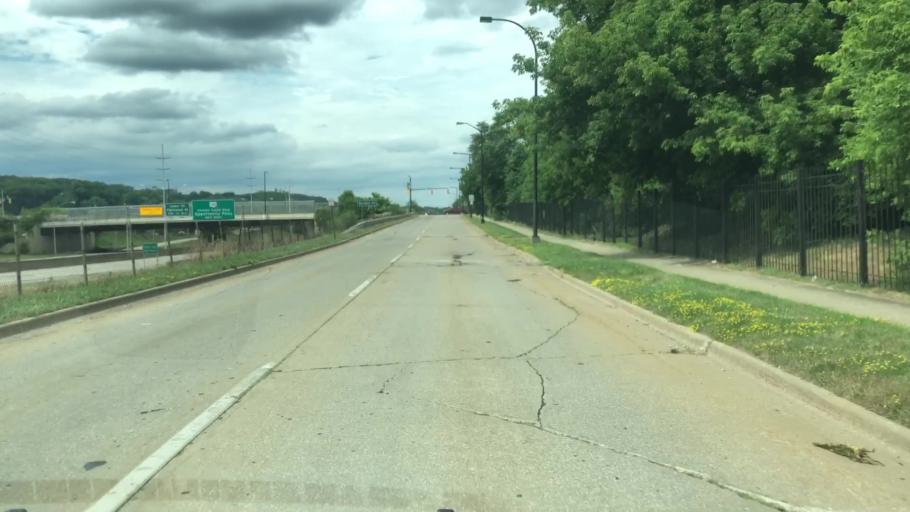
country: US
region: Ohio
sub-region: Summit County
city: Akron
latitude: 41.0688
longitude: -81.5372
